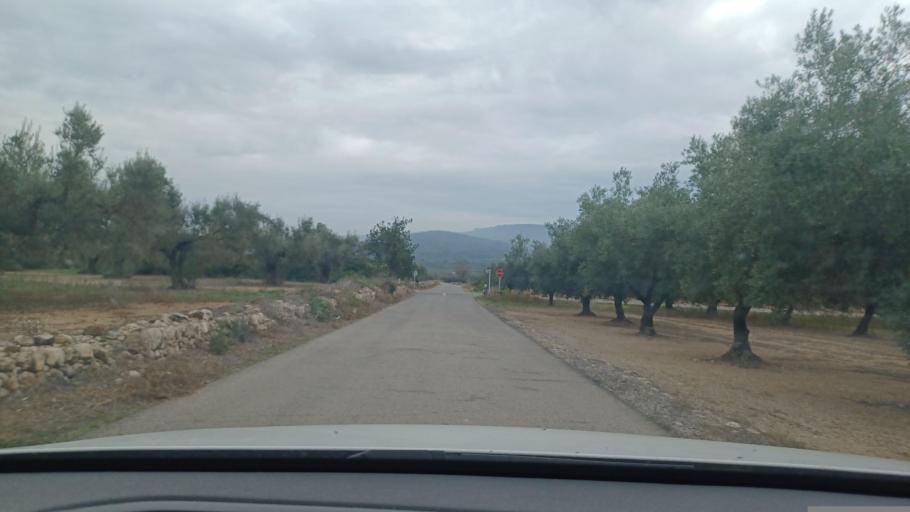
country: ES
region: Catalonia
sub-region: Provincia de Tarragona
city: Santa Barbara
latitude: 40.6667
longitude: 0.4465
